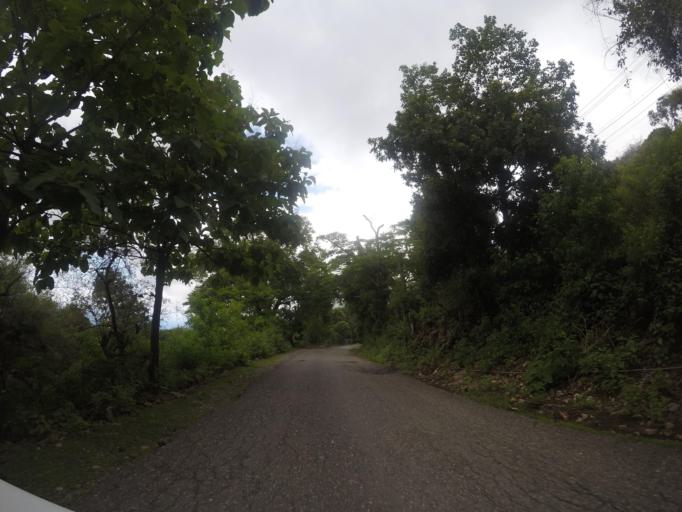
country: TL
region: Bobonaro
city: Maliana
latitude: -8.9611
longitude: 125.0298
